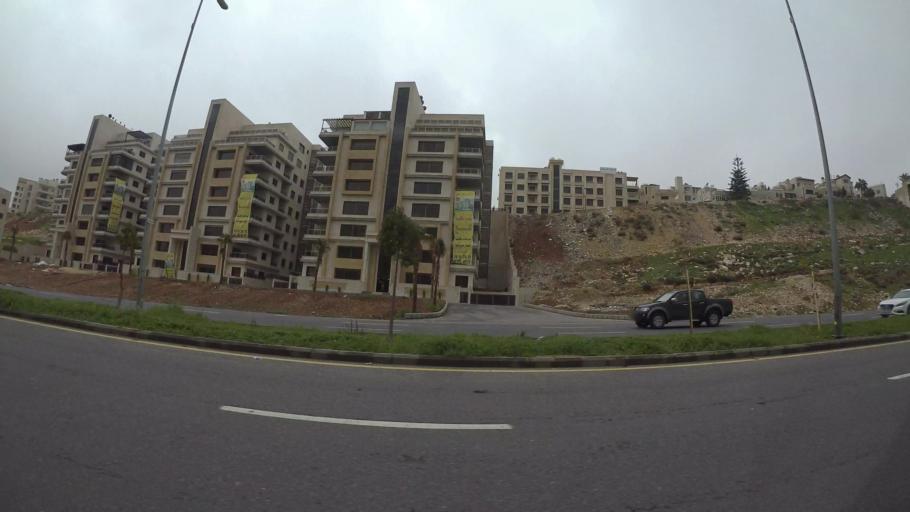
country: JO
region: Amman
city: Al Bunayyat ash Shamaliyah
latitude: 31.9386
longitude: 35.8708
